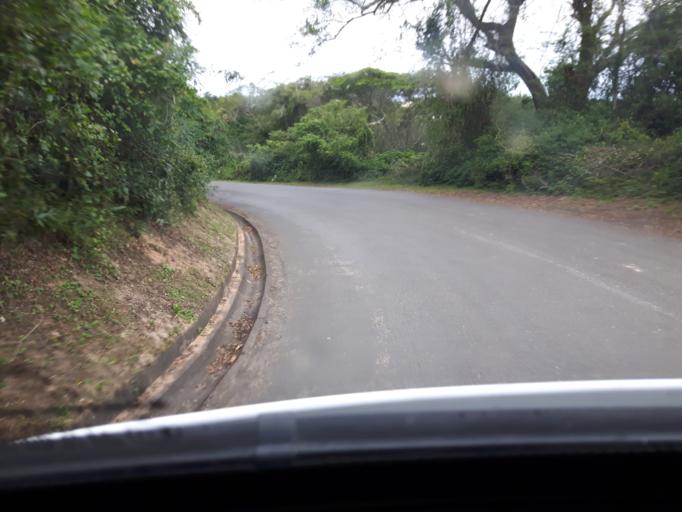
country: ZA
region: KwaZulu-Natal
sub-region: uMkhanyakude District Municipality
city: Mtubatuba
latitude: -28.3878
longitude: 32.4102
